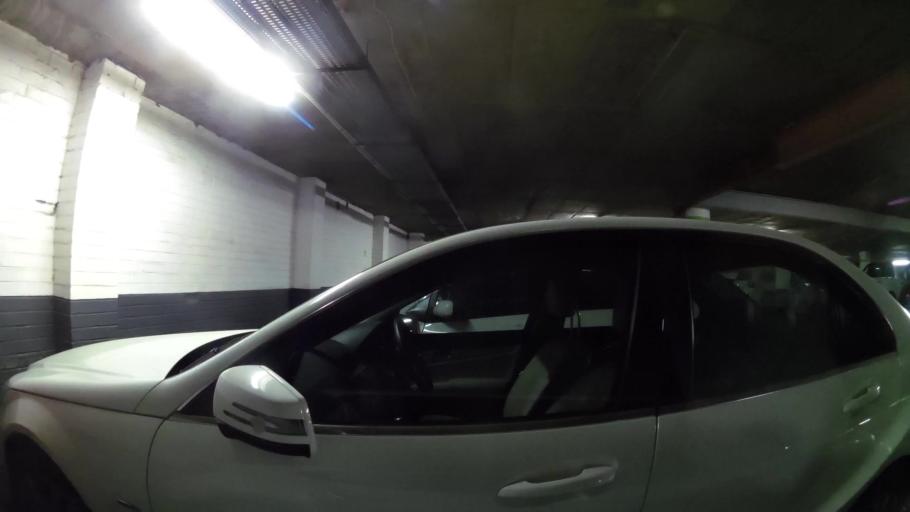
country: ZA
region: Orange Free State
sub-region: Mangaung Metropolitan Municipality
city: Bloemfontein
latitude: -29.0877
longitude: 26.2123
